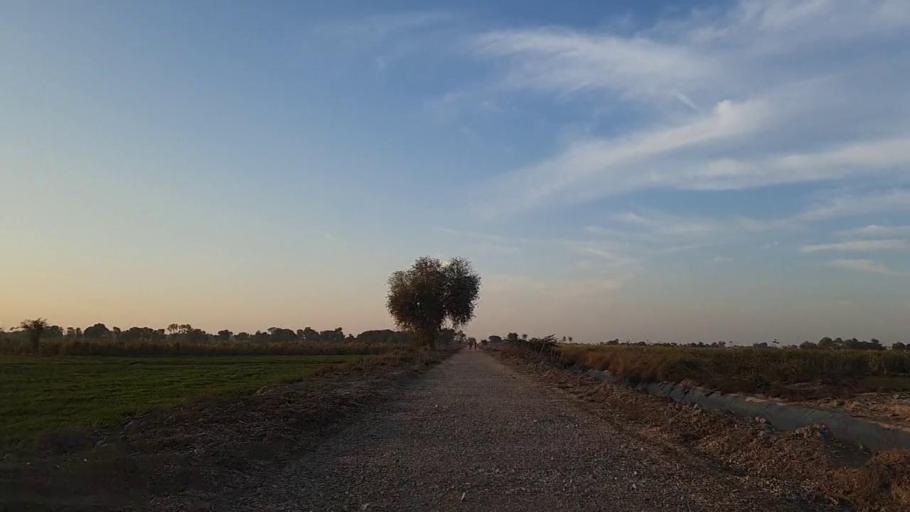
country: PK
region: Sindh
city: Bandhi
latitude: 26.6178
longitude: 68.3523
